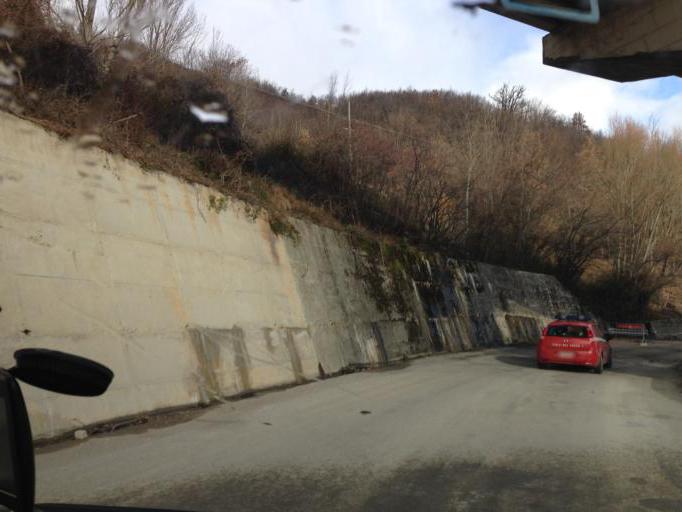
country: IT
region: The Marches
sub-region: Provincia di Ascoli Piceno
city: Arquata del Tronto
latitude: 42.7556
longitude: 13.2760
